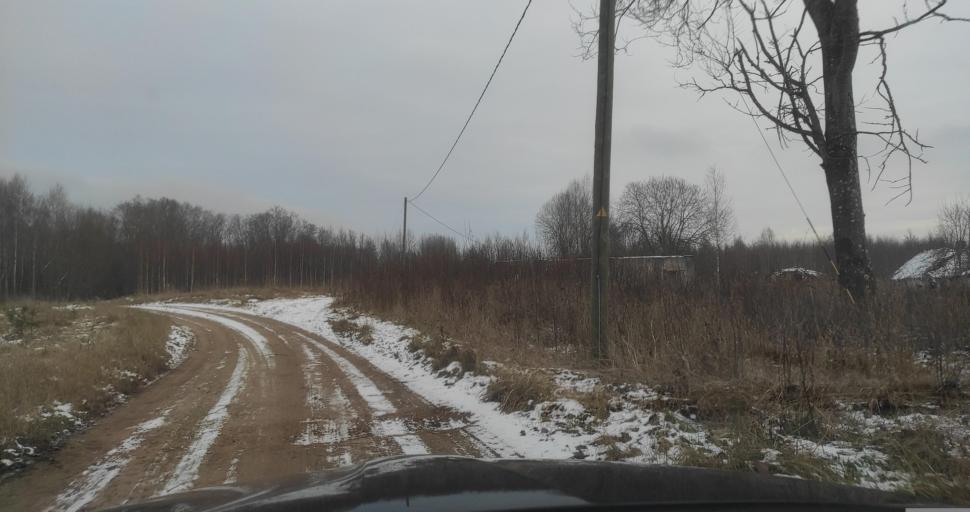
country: LV
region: Alsunga
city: Alsunga
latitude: 56.9578
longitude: 21.6433
